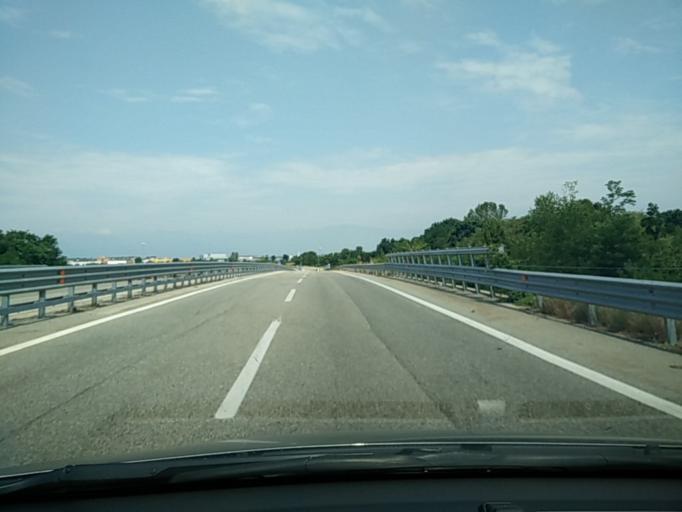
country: IT
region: Piedmont
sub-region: Provincia di Torino
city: Volpiano
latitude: 45.1792
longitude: 7.8015
